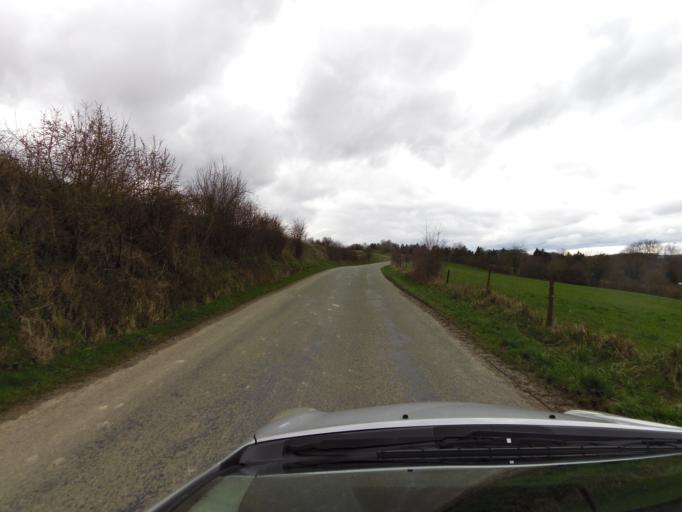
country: FR
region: Picardie
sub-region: Departement de la Somme
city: Bray-sur-Somme
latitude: 49.9361
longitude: 2.8183
